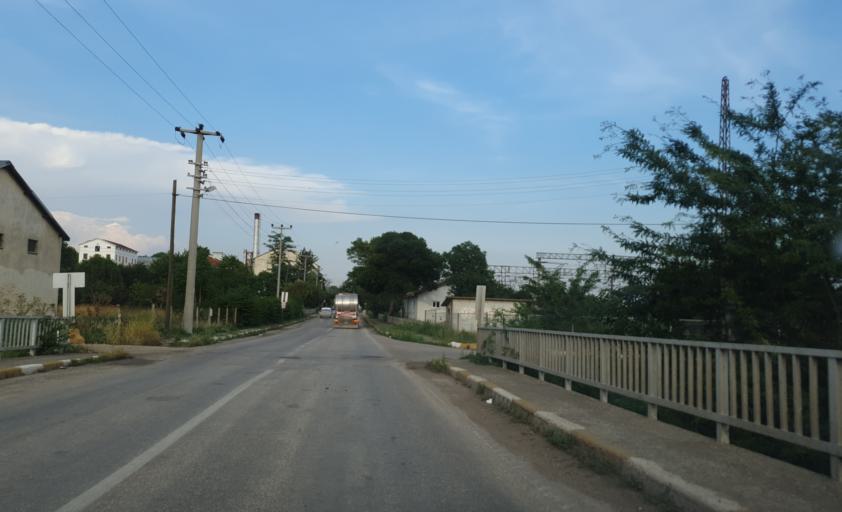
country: TR
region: Kirklareli
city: Babaeski
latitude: 41.3669
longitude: 27.1394
